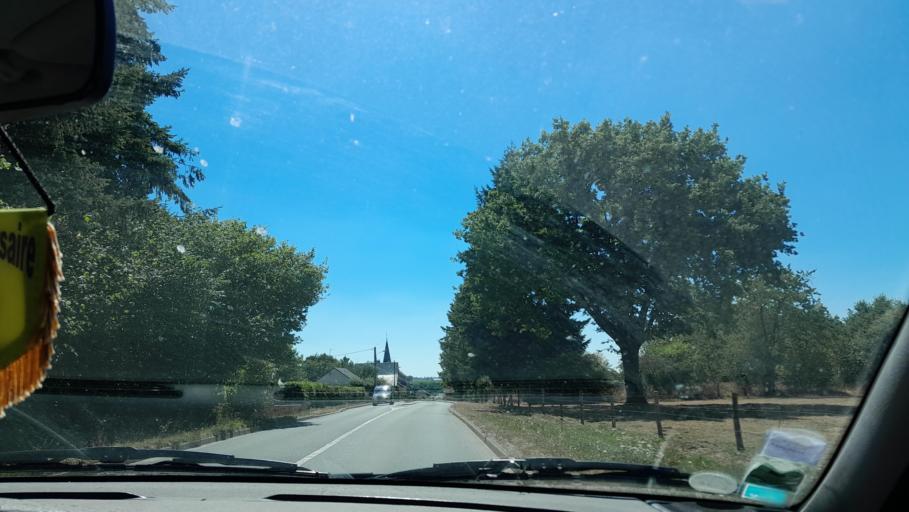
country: FR
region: Pays de la Loire
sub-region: Departement de la Mayenne
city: Congrier
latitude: 47.8822
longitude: -1.1248
